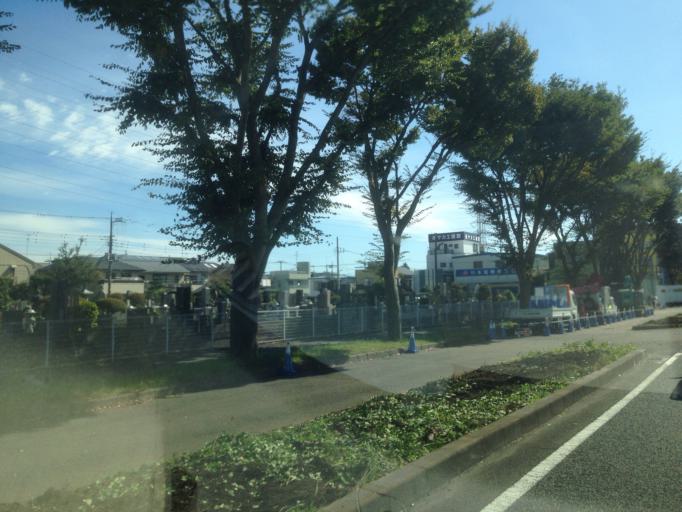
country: JP
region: Tokyo
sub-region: Machida-shi
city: Machida
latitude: 35.5699
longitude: 139.3807
